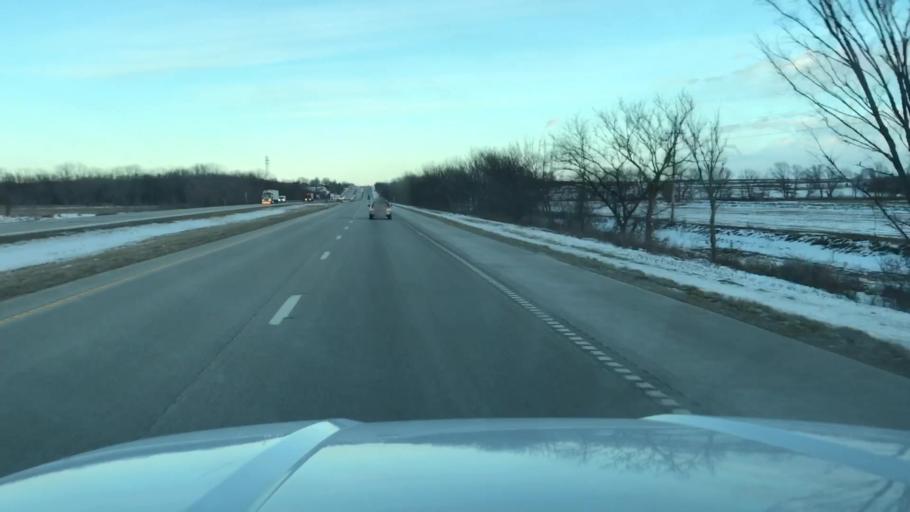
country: US
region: Missouri
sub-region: Clinton County
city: Gower
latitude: 39.7474
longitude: -94.6678
